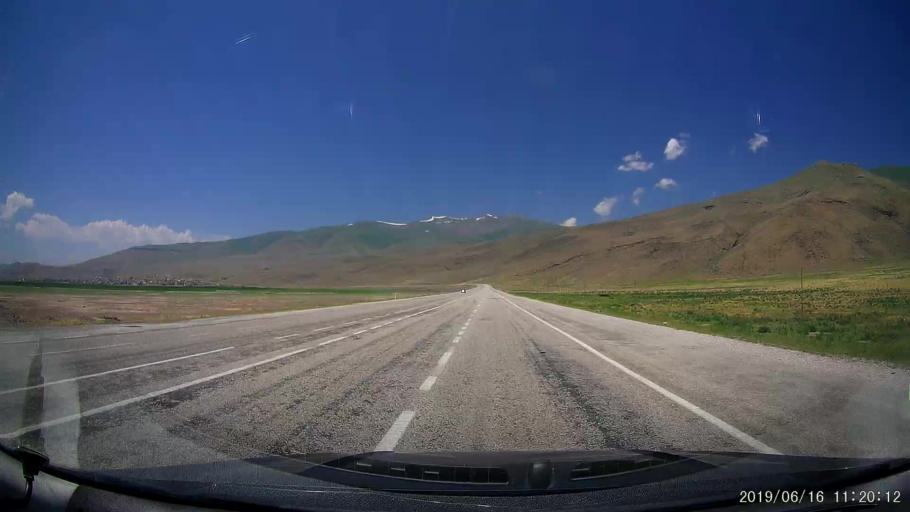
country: TR
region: Agri
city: Dogubayazit
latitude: 39.6975
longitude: 44.0966
